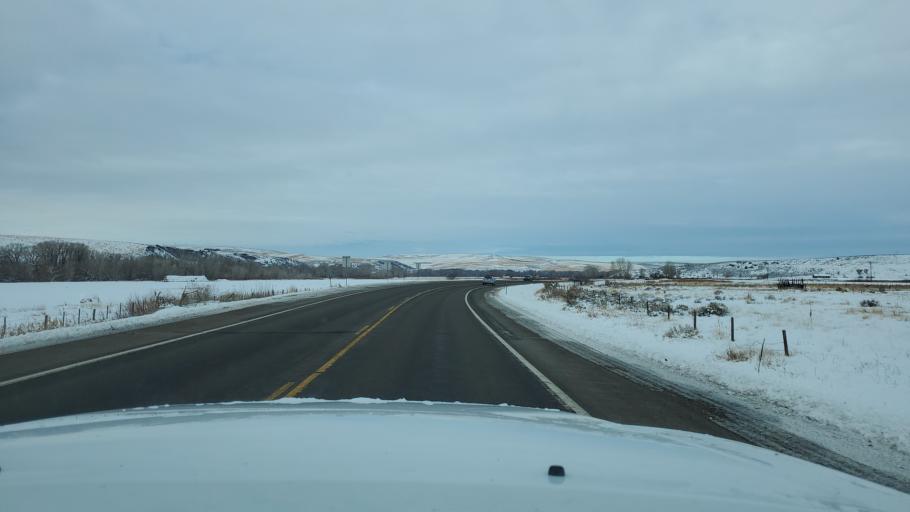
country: US
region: Colorado
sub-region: Routt County
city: Hayden
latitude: 40.4922
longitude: -107.3440
